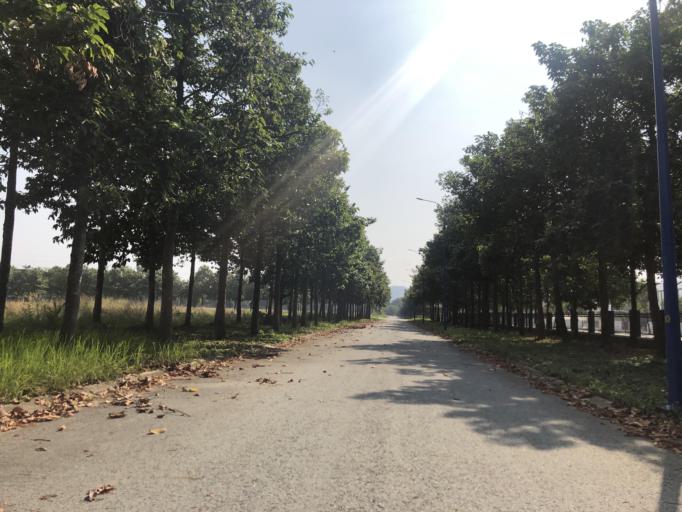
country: VN
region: Binh Duong
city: Thu Dau Mot
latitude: 11.0513
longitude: 106.6642
